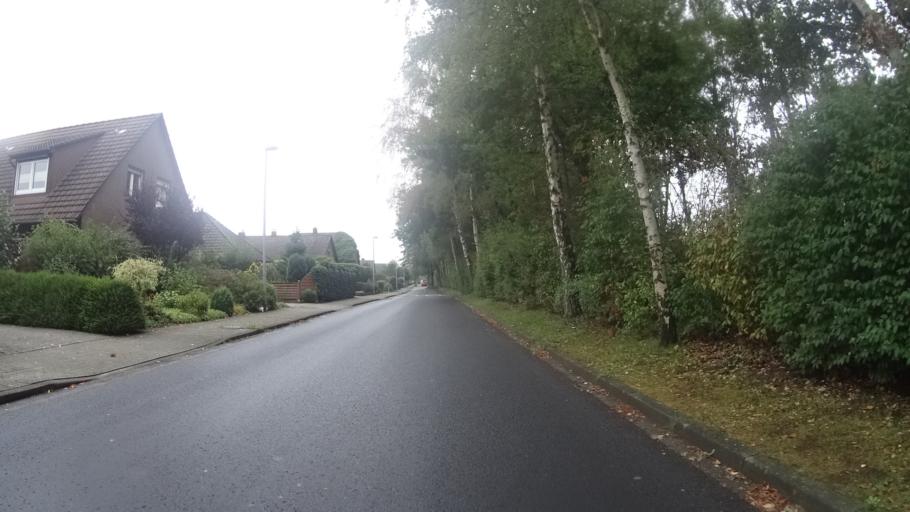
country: DE
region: Lower Saxony
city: Leer
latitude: 53.2443
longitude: 7.4766
